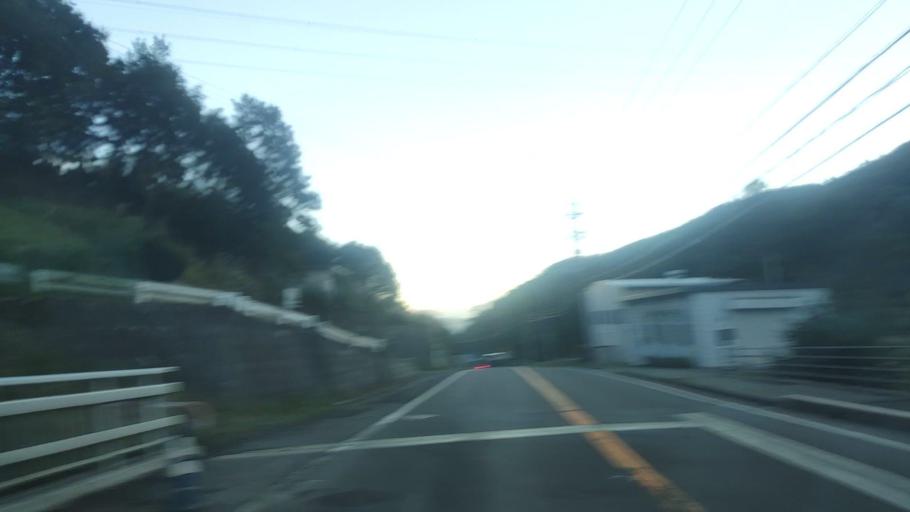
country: JP
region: Nagano
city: Suwa
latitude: 36.1153
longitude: 138.1000
